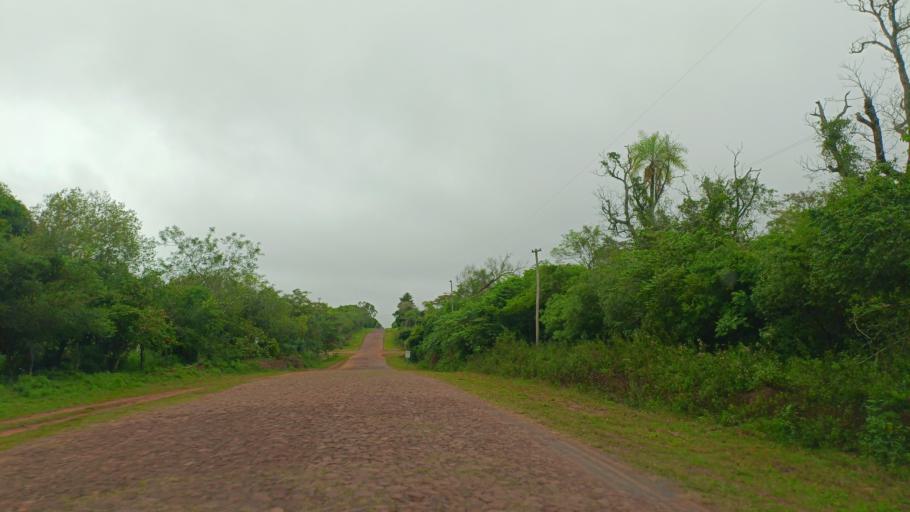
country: PY
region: Misiones
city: Santa Maria
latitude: -26.8706
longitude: -57.0117
